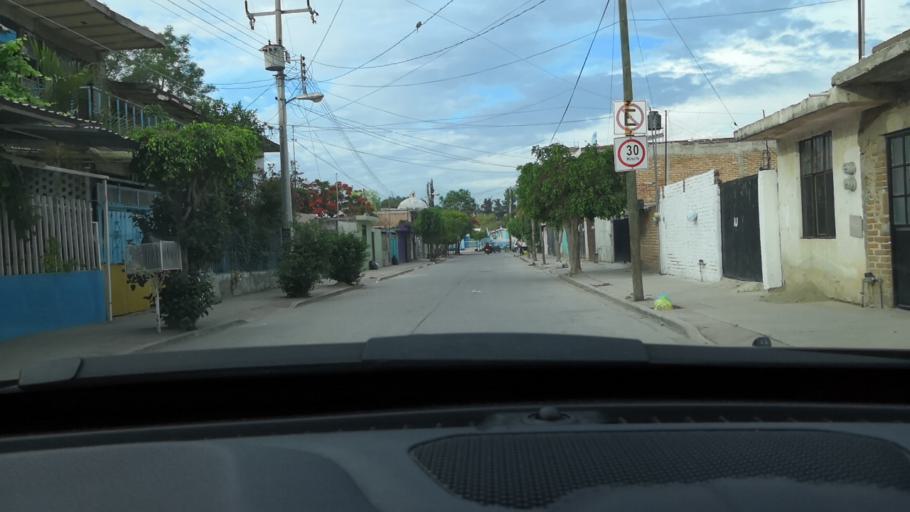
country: MX
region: Guanajuato
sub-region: Leon
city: Fraccionamiento Paraiso Real
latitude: 21.0931
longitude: -101.6051
